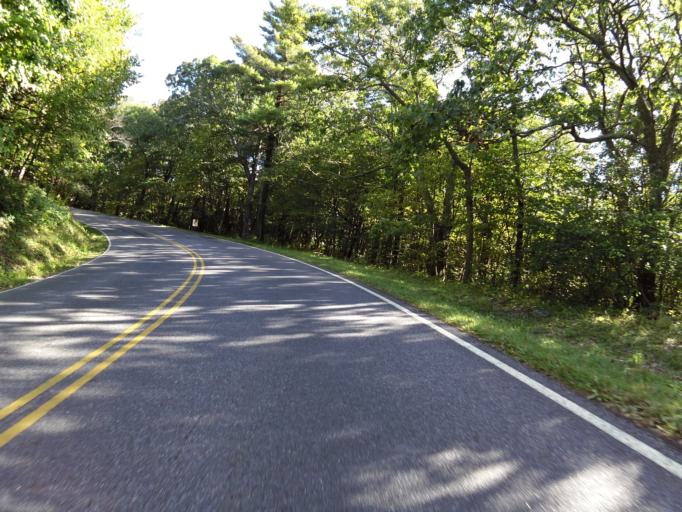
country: US
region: Virginia
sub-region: Page County
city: Stanley
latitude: 38.5451
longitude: -78.4029
